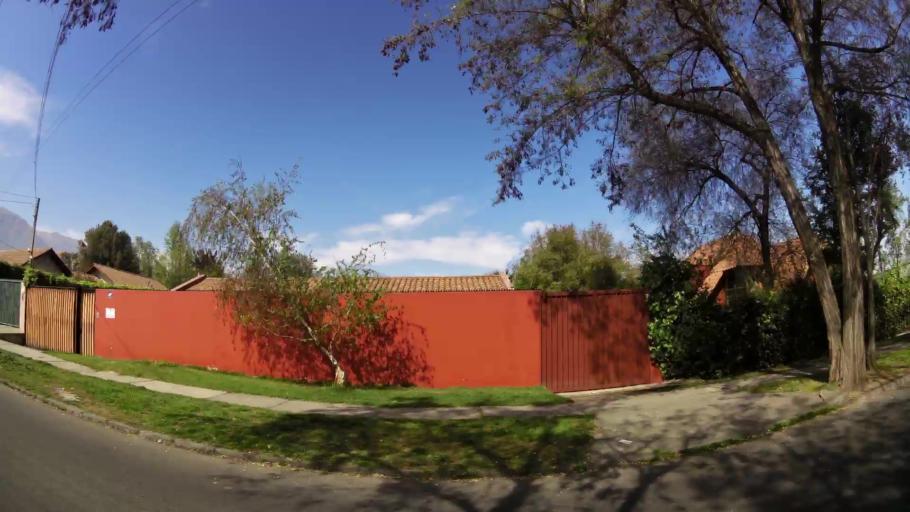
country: CL
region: Santiago Metropolitan
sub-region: Provincia de Santiago
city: Villa Presidente Frei, Nunoa, Santiago, Chile
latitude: -33.4381
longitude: -70.5448
